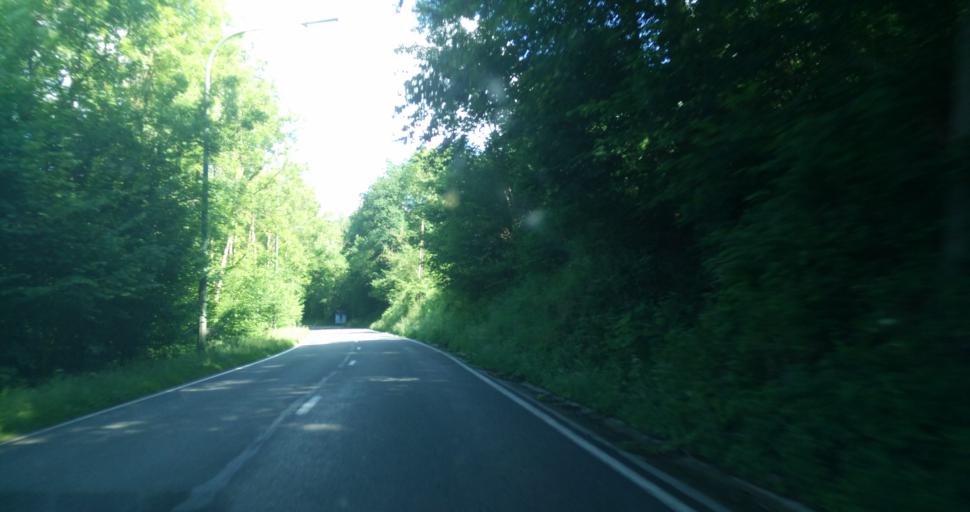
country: BE
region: Wallonia
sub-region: Province du Luxembourg
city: La Roche-en-Ardenne
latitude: 50.1870
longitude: 5.5432
